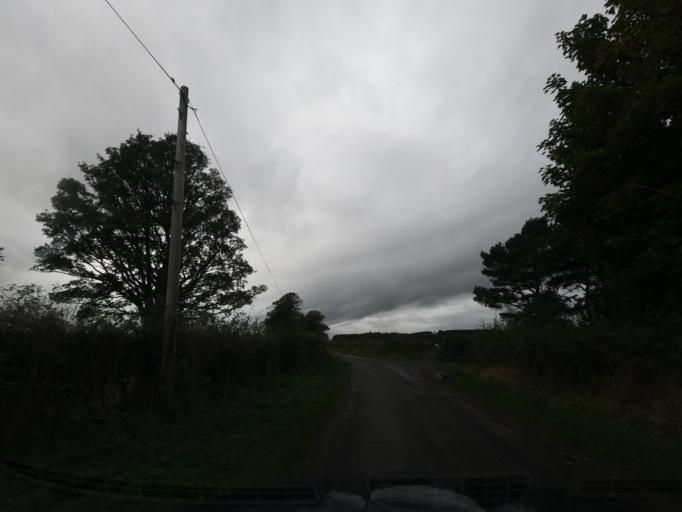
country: GB
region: England
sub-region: Northumberland
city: Doddington
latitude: 55.6005
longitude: -2.0316
